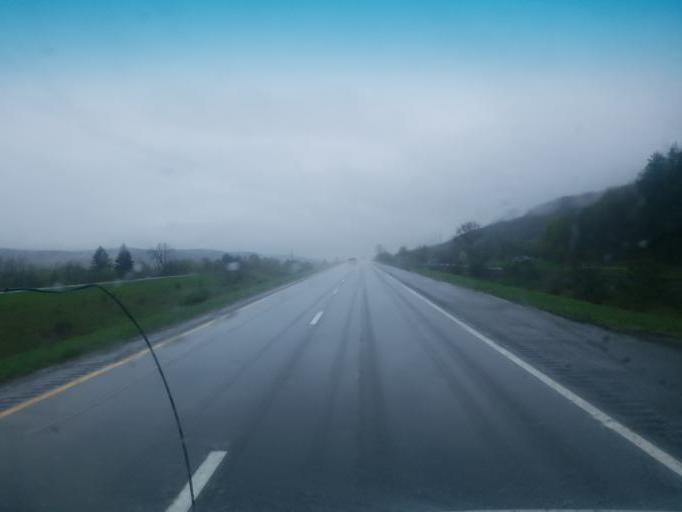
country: US
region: New York
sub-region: Cattaraugus County
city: Olean
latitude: 42.1531
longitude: -78.4058
